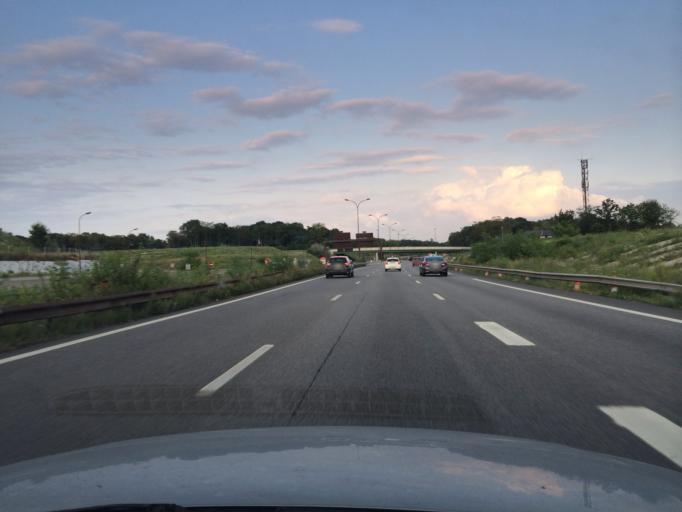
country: FR
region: Ile-de-France
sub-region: Departement des Yvelines
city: Rocquencourt
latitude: 48.8411
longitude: 2.1059
